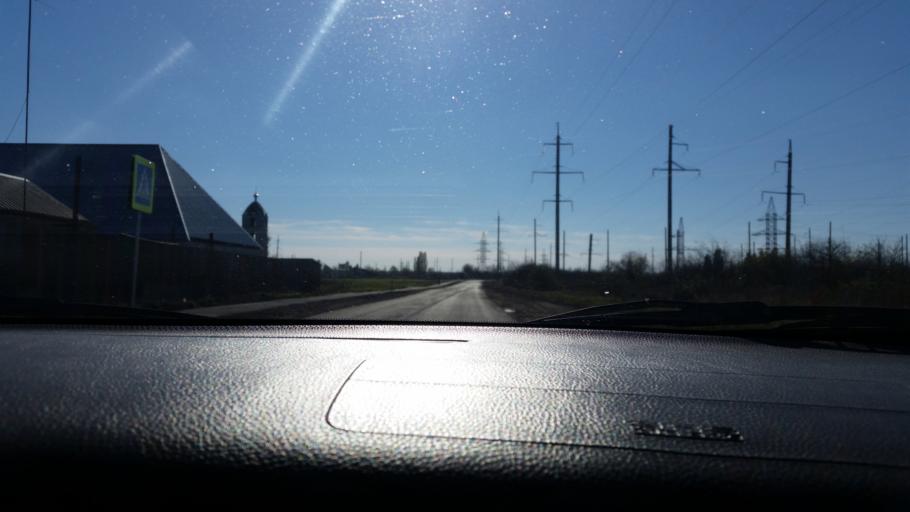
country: RU
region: Lipetsk
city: Gryazi
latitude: 52.4692
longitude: 39.9432
